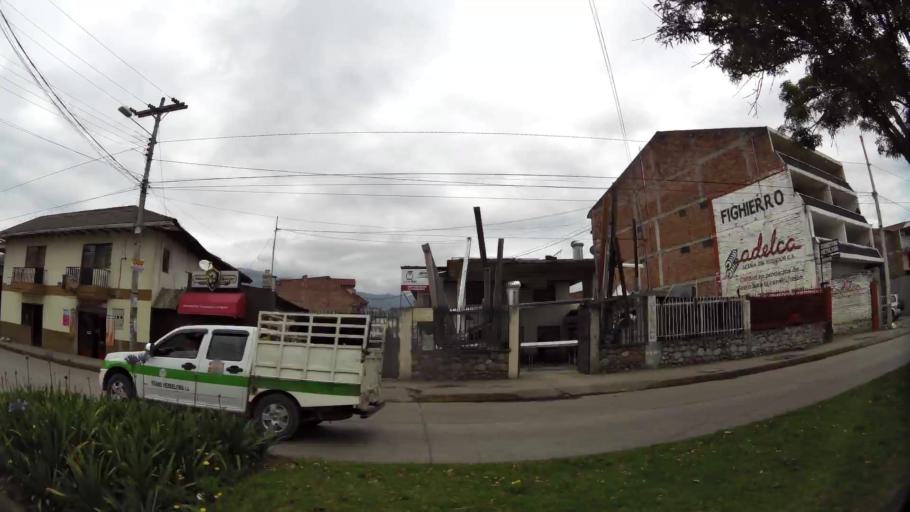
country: EC
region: Azuay
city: Cuenca
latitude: -2.9180
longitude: -79.0347
